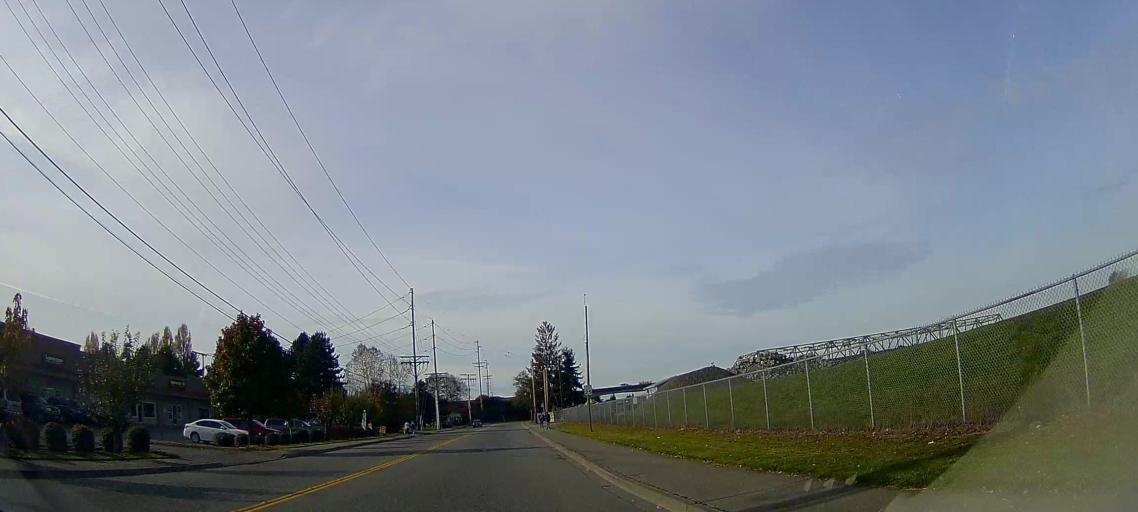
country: US
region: Washington
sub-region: Skagit County
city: Mount Vernon
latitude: 48.4432
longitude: -122.3380
